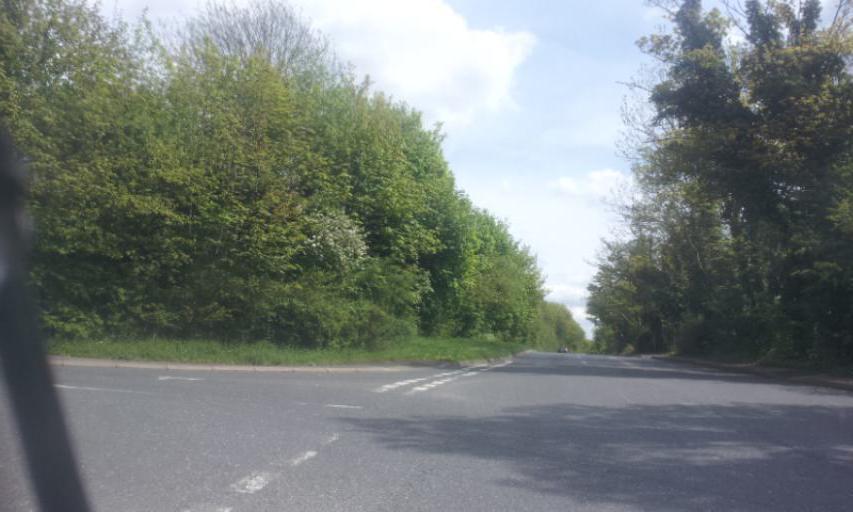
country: GB
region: England
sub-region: Kent
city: Longfield
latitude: 51.3929
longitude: 0.3248
